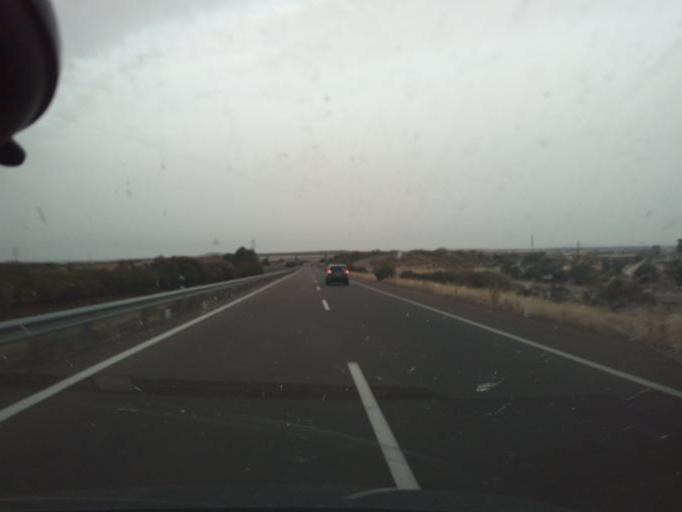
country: ES
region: Extremadura
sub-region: Provincia de Badajoz
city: San Pedro de Merida
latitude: 38.9495
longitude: -6.2148
